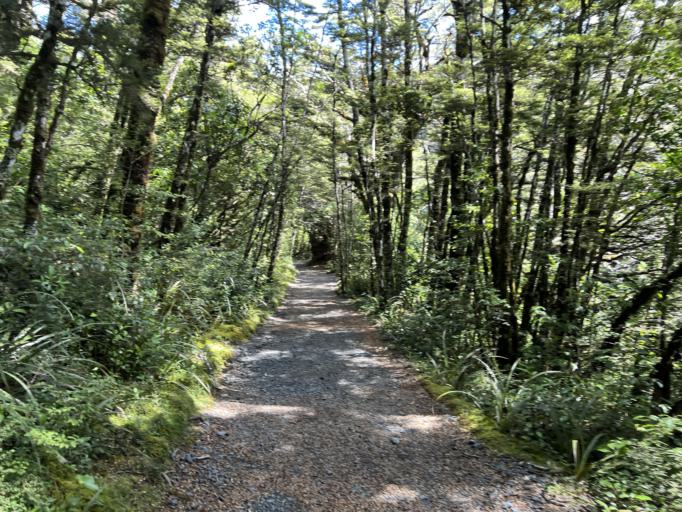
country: NZ
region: Manawatu-Wanganui
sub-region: Ruapehu District
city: Waiouru
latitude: -39.2011
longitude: 175.5487
